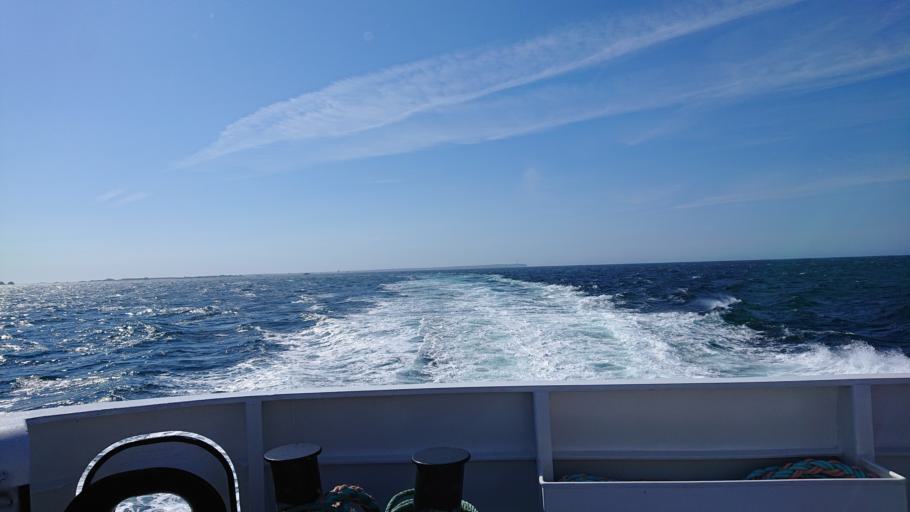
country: FR
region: Brittany
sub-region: Departement du Finistere
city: Le Conquet
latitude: 48.4128
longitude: -4.9358
